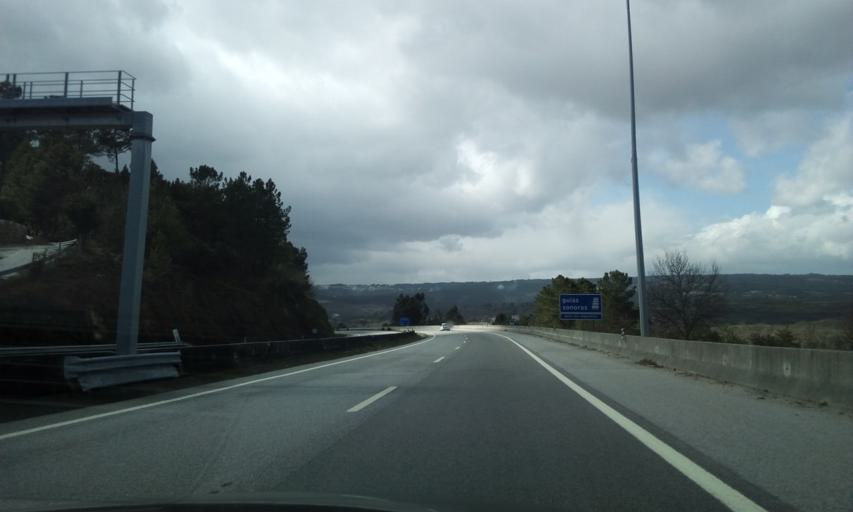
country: PT
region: Viseu
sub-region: Mangualde
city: Mangualde
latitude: 40.6321
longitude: -7.8056
